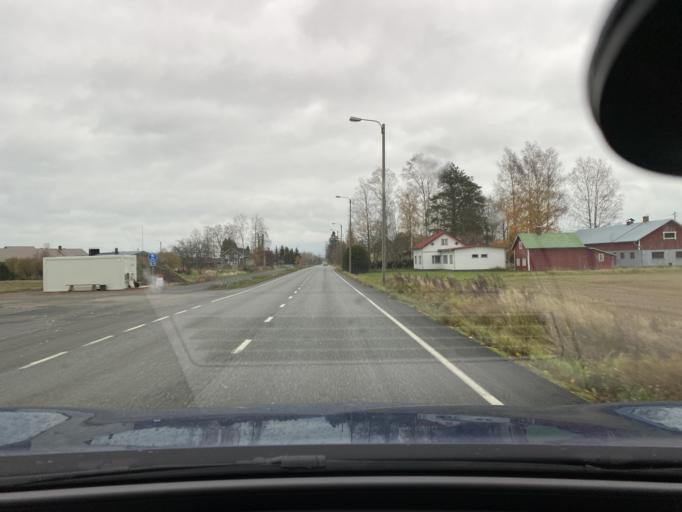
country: FI
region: Satakunta
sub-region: Rauma
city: Saekylae
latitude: 61.0640
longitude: 22.5104
